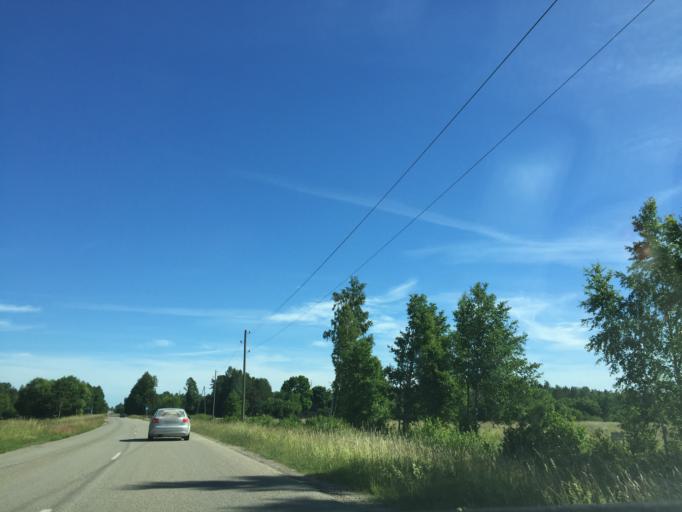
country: LV
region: Rojas
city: Roja
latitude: 57.4639
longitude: 22.8749
